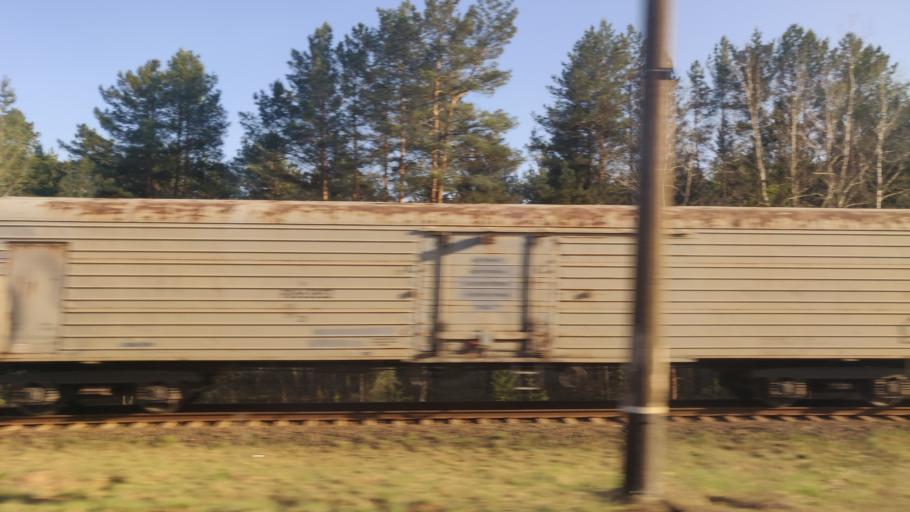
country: LT
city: Baltoji Voke
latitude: 54.6287
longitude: 25.1675
